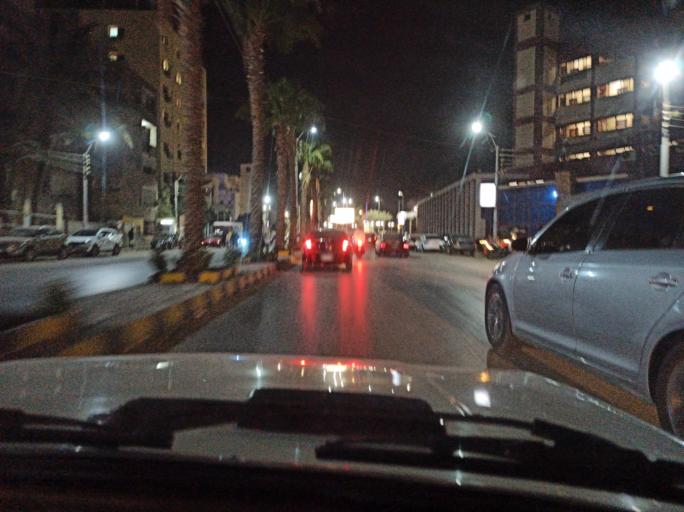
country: EG
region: Muhafazat Bani Suwayf
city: Bani Suwayf
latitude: 29.0735
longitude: 31.1140
